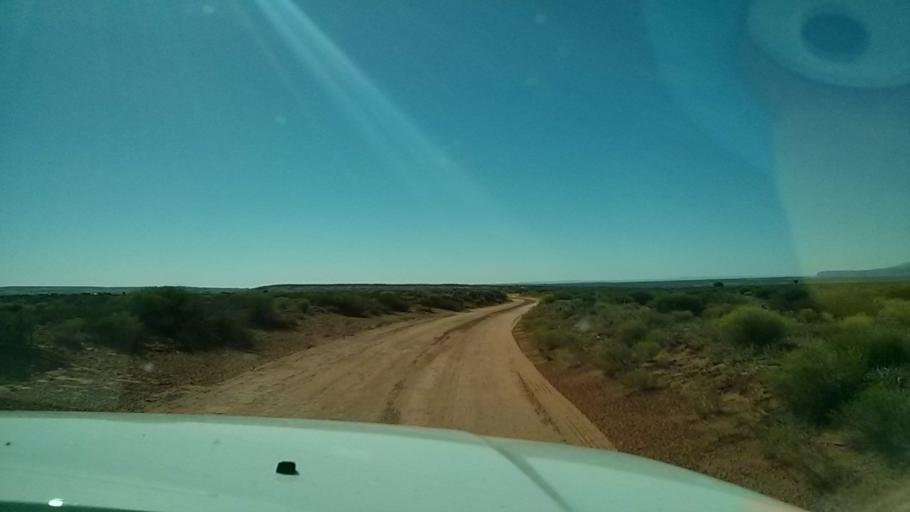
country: US
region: Arizona
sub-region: Coconino County
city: Page
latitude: 37.4657
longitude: -111.2158
